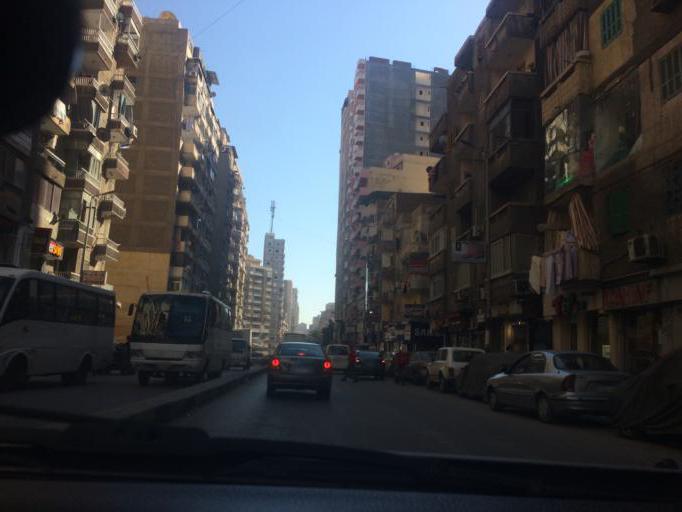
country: EG
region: Alexandria
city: Alexandria
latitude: 31.2634
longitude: 29.9951
